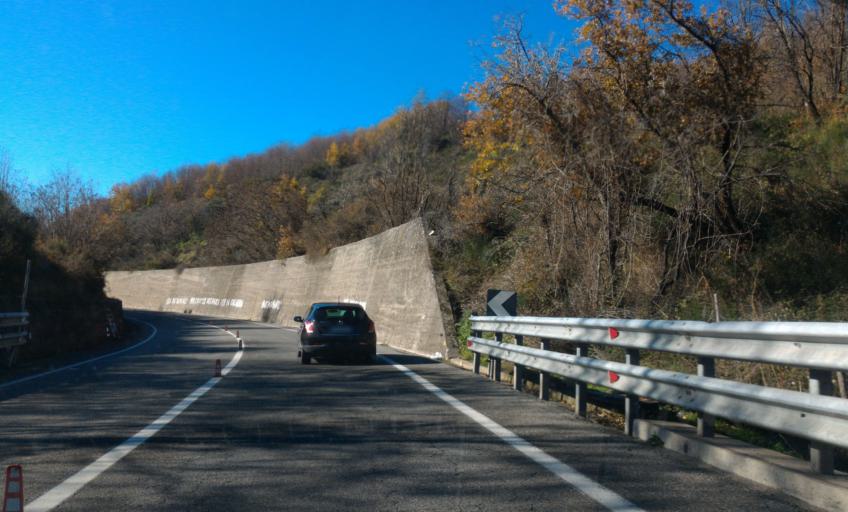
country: IT
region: Calabria
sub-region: Provincia di Cosenza
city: Celico
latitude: 39.3167
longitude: 16.3353
